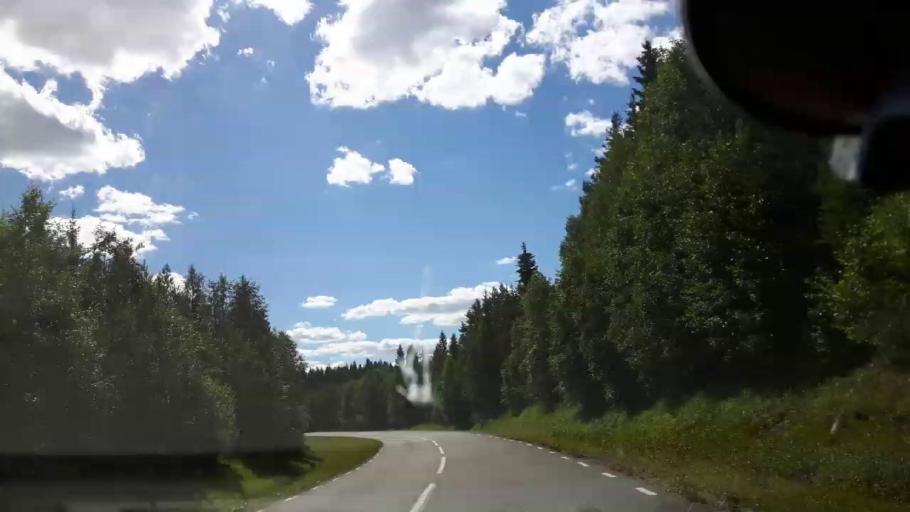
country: SE
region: Jaemtland
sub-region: Ragunda Kommun
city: Hammarstrand
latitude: 62.8550
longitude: 16.1897
